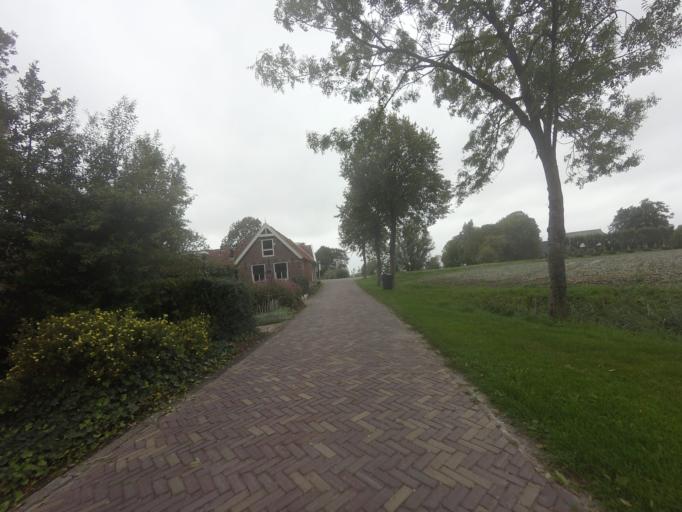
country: NL
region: Friesland
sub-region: Gemeente Ferwerderadiel
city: Ferwert
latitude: 53.3363
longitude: 5.8527
